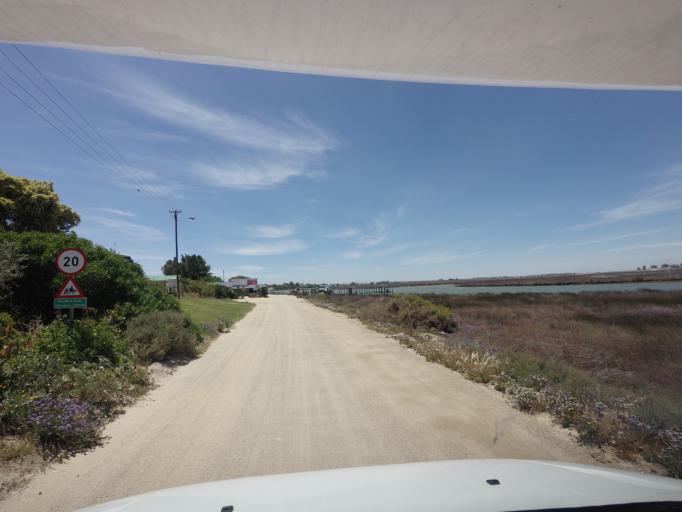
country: ZA
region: Western Cape
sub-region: West Coast District Municipality
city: Vredenburg
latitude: -32.7881
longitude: 18.1842
